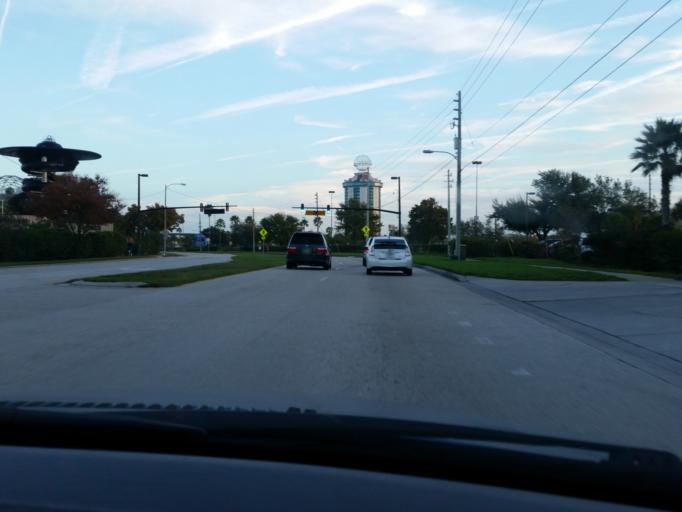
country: US
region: Florida
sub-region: Orange County
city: Tangelo Park
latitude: 28.4580
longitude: -81.4641
